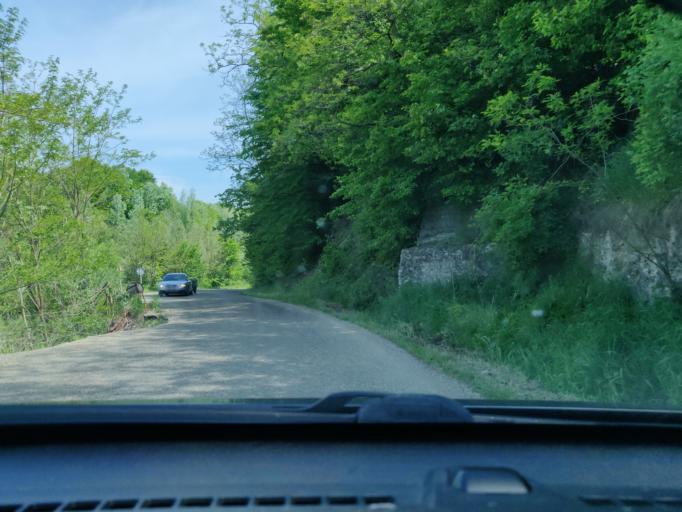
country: RO
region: Vrancea
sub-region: Comuna Vidra
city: Vidra
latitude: 45.9362
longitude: 26.8816
